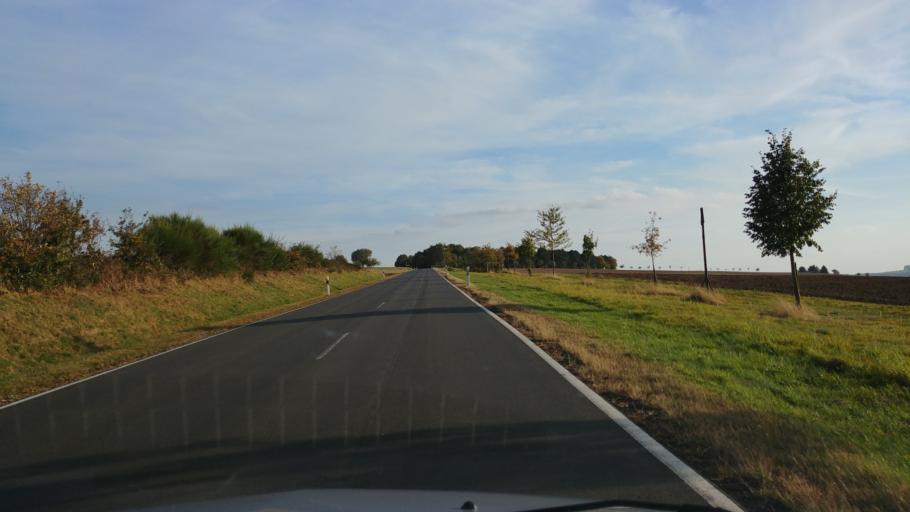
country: DE
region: Rheinland-Pfalz
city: Merschbach
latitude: 49.8203
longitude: 7.0331
